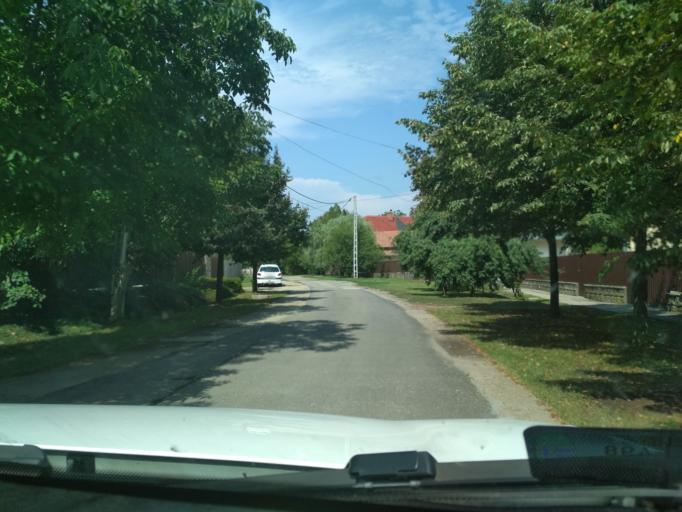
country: HU
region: Jasz-Nagykun-Szolnok
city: Abadszalok
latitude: 47.4740
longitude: 20.5861
